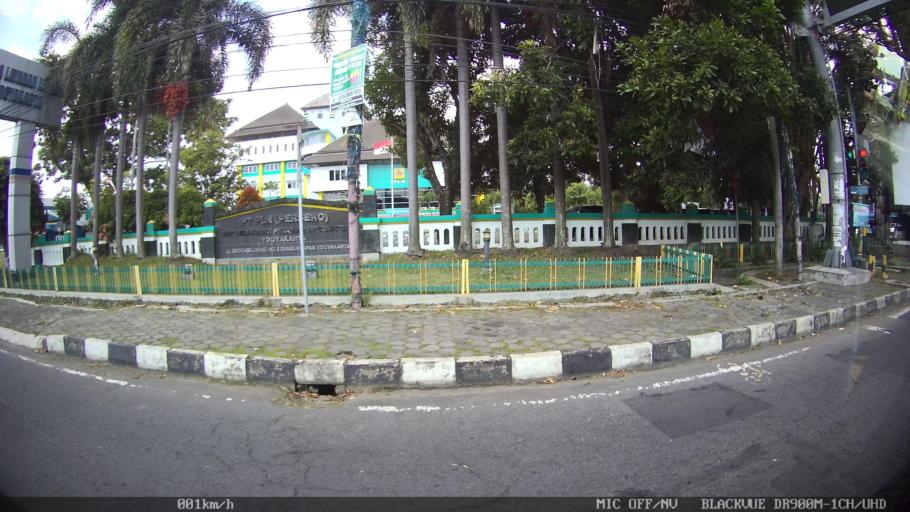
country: ID
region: Daerah Istimewa Yogyakarta
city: Yogyakarta
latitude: -7.8103
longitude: 110.4022
